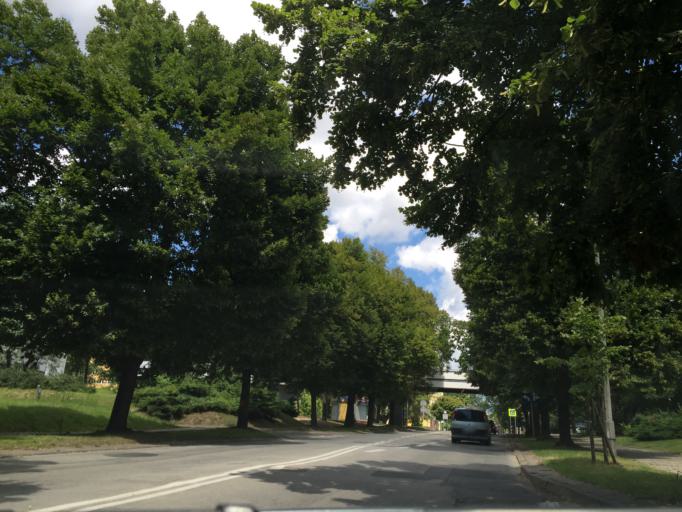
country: PL
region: Lublin Voivodeship
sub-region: Powiat lubelski
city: Lublin
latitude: 51.2449
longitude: 22.5395
